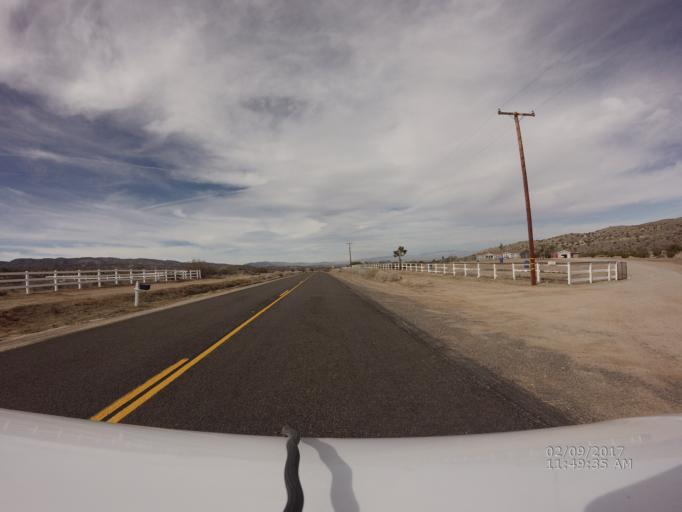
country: US
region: California
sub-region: Los Angeles County
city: Littlerock
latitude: 34.4830
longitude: -117.9212
